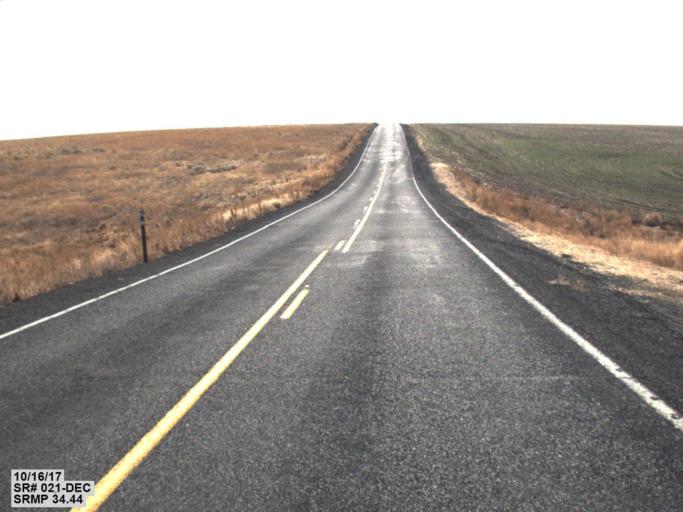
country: US
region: Washington
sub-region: Adams County
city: Ritzville
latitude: 47.0491
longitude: -118.6631
